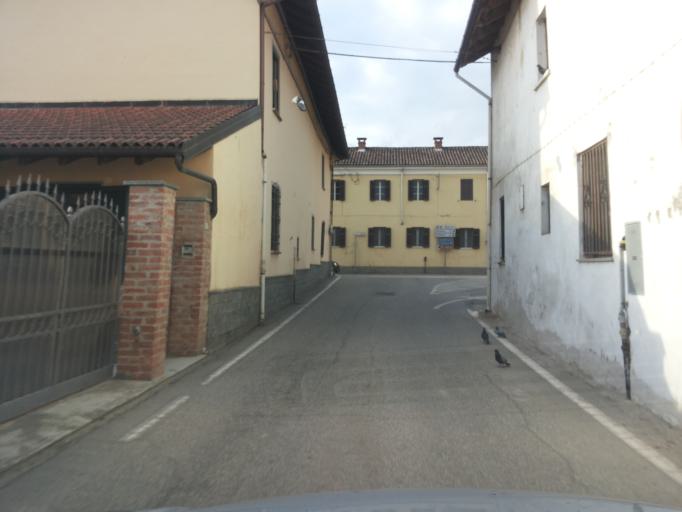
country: IT
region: Piedmont
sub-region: Provincia di Vercelli
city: Motta De Conti
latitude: 45.1914
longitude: 8.5202
